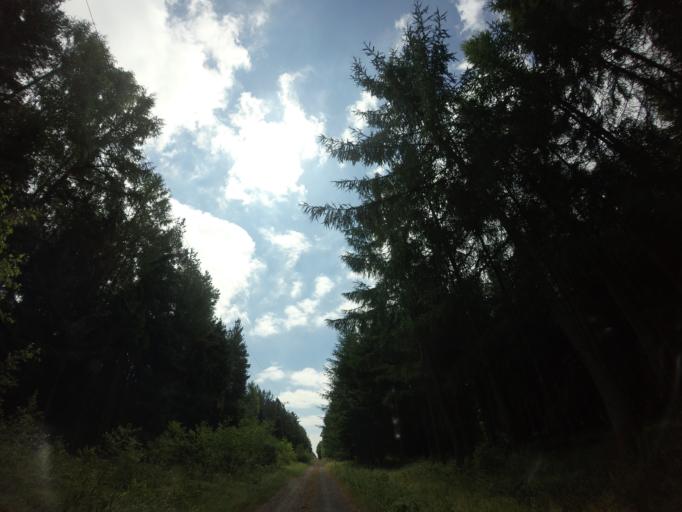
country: PL
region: West Pomeranian Voivodeship
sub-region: Powiat choszczenski
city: Krzecin
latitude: 52.9917
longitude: 15.4804
